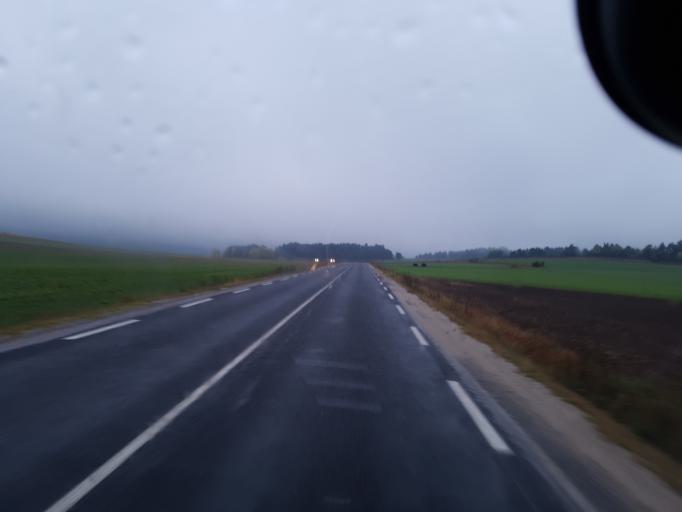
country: FR
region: Languedoc-Roussillon
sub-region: Departement de la Lozere
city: Langogne
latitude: 44.8333
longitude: 3.8625
